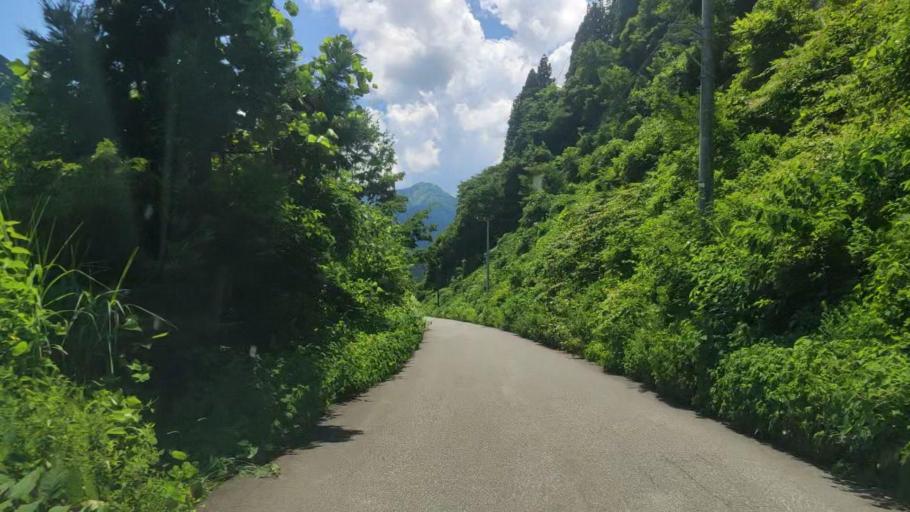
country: JP
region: Fukui
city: Ono
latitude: 35.8926
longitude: 136.5066
